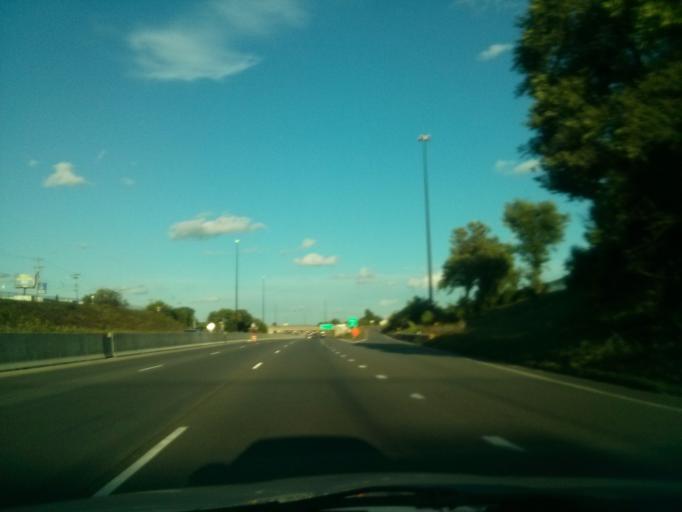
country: US
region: Minnesota
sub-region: Hennepin County
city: Richfield
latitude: 44.8618
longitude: -93.2831
